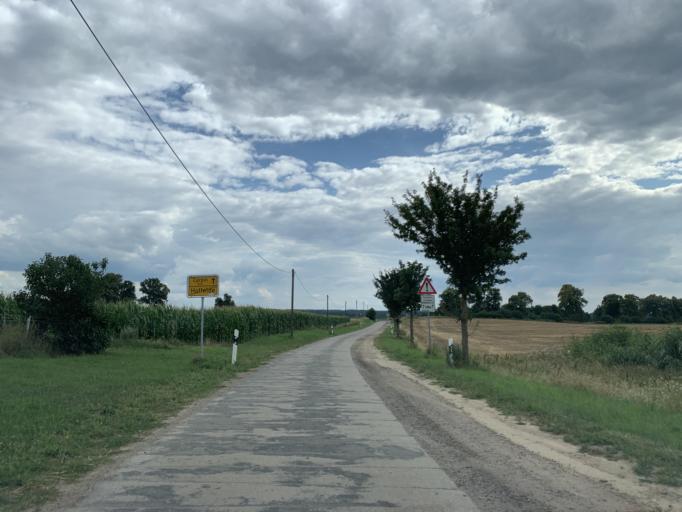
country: DE
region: Mecklenburg-Vorpommern
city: Blankensee
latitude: 53.3730
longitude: 13.2905
